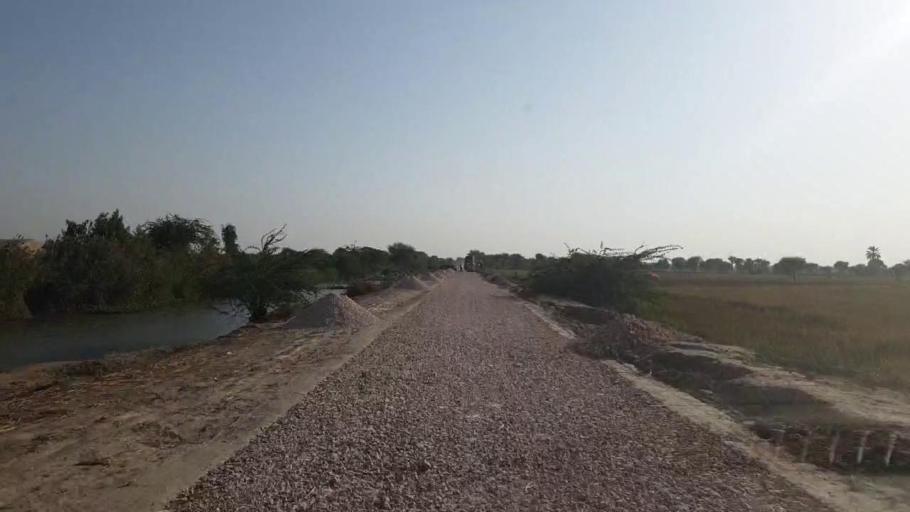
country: PK
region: Sindh
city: Talhar
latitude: 24.9327
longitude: 68.7496
